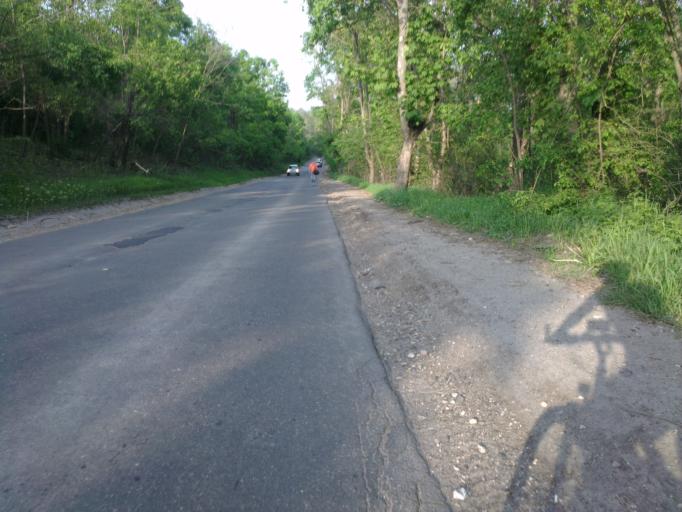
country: MD
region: Chisinau
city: Stauceni
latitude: 47.0604
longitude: 28.8790
